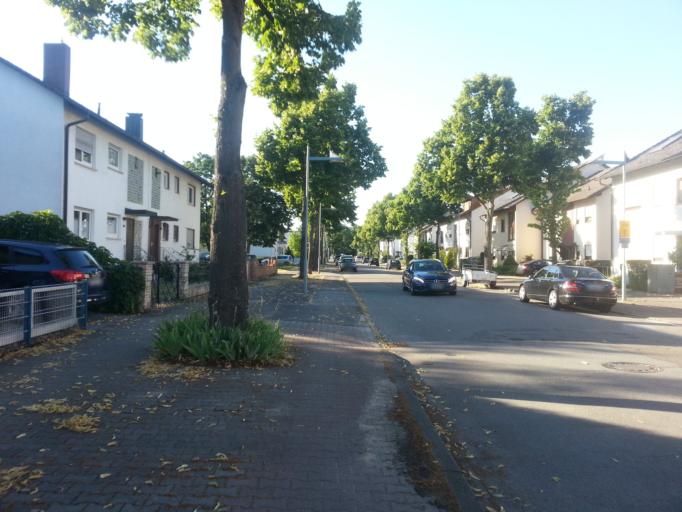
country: DE
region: Baden-Wuerttemberg
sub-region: Karlsruhe Region
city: Mannheim
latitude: 49.5276
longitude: 8.5104
